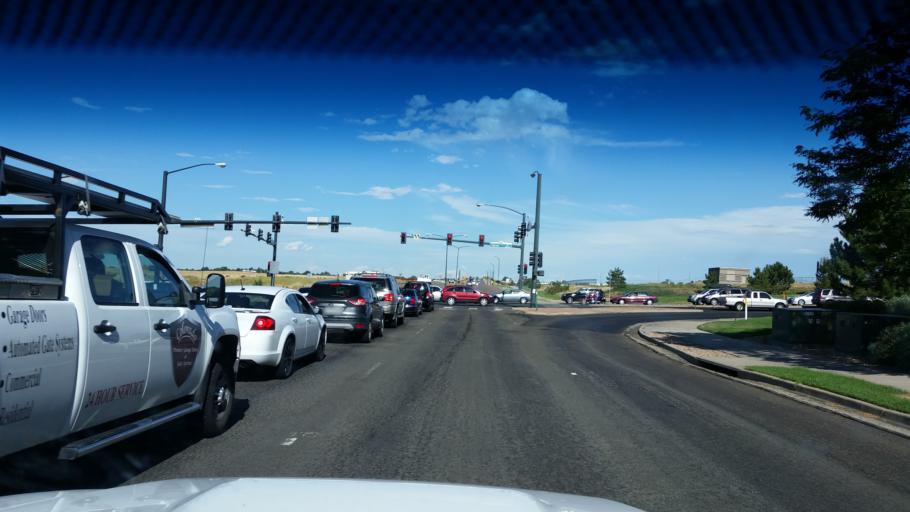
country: US
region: Colorado
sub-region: Adams County
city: Northglenn
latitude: 39.9285
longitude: -104.9977
